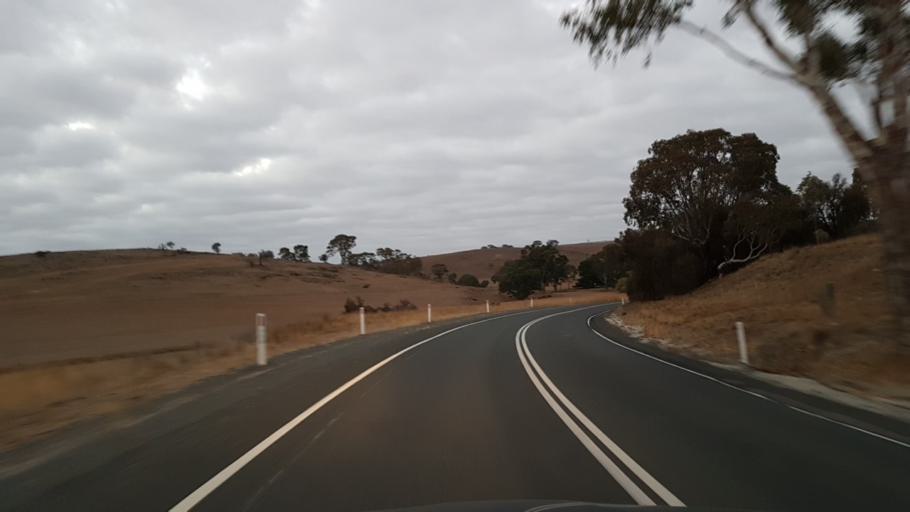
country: AU
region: South Australia
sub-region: Mount Barker
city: Nairne
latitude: -35.0369
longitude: 138.9866
